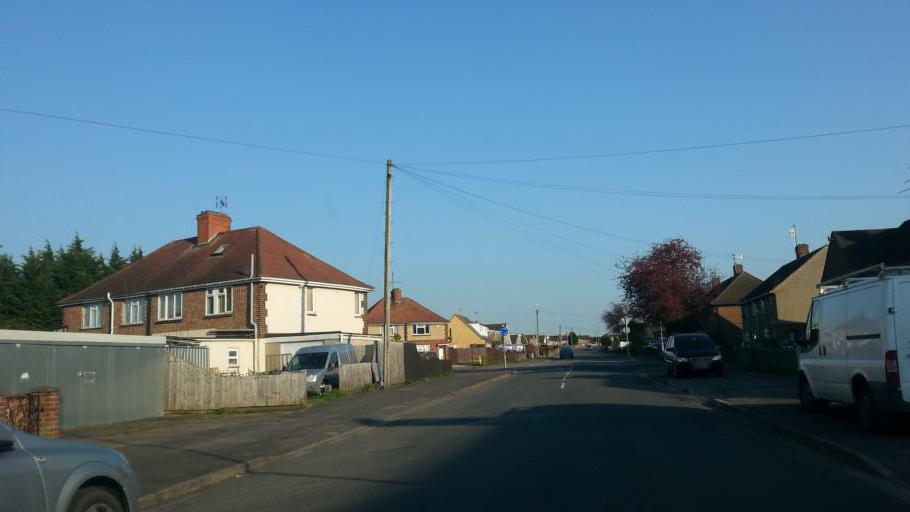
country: GB
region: England
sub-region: Northamptonshire
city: Rushden
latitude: 52.2880
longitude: -0.6183
